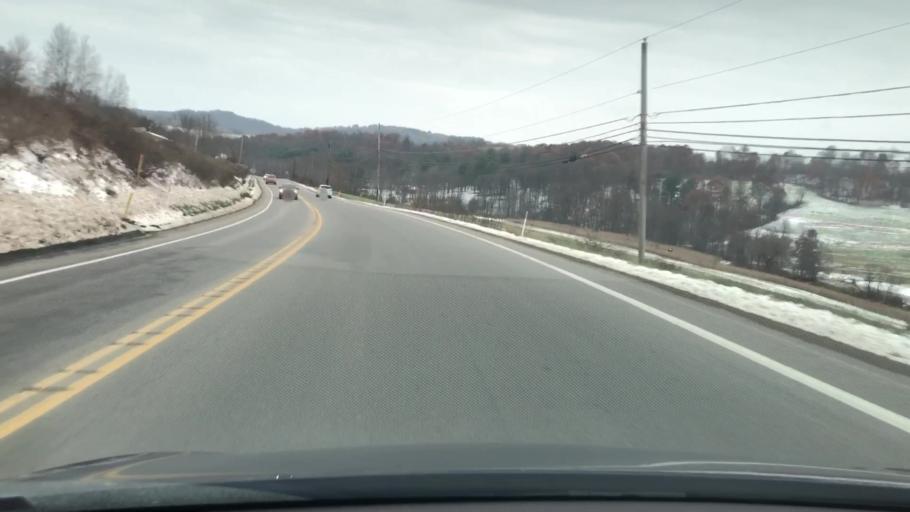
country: US
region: Pennsylvania
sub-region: Jefferson County
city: Brookville
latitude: 41.1105
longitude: -79.2123
